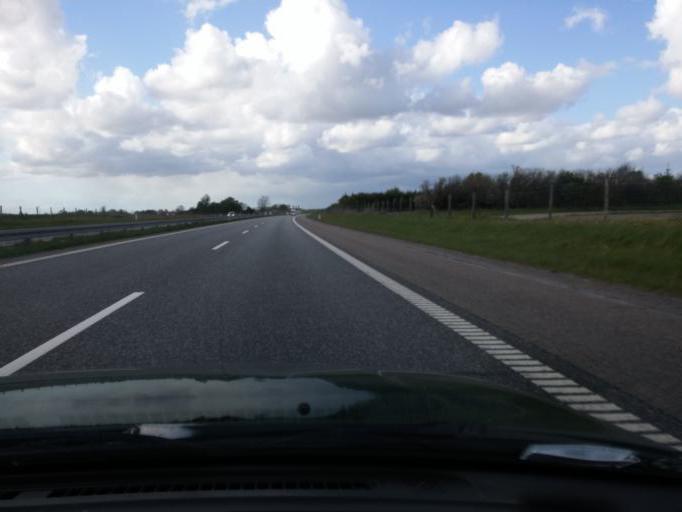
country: DK
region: South Denmark
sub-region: Faaborg-Midtfyn Kommune
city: Arslev
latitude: 55.2972
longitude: 10.4382
